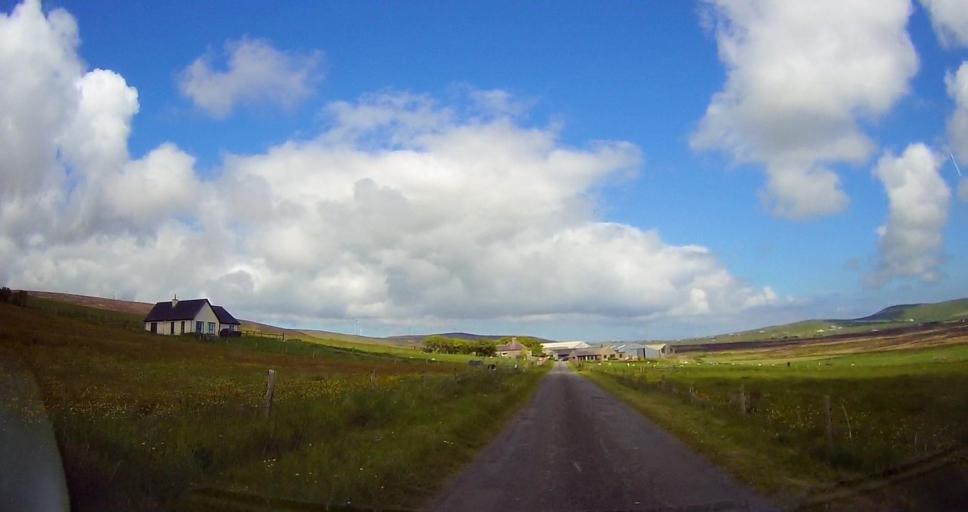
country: GB
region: Scotland
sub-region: Orkney Islands
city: Orkney
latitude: 59.0553
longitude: -3.1026
